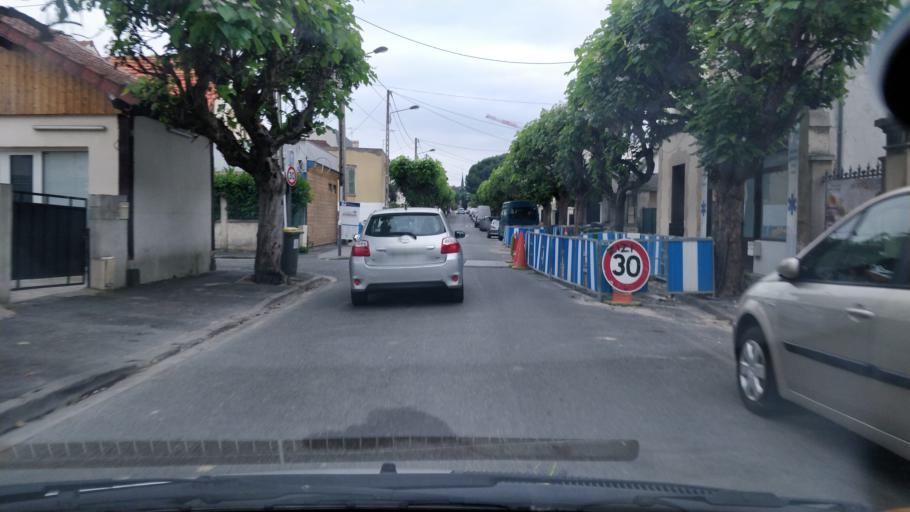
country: FR
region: Ile-de-France
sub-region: Departement de Seine-Saint-Denis
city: Le Raincy
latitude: 48.9052
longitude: 2.5248
